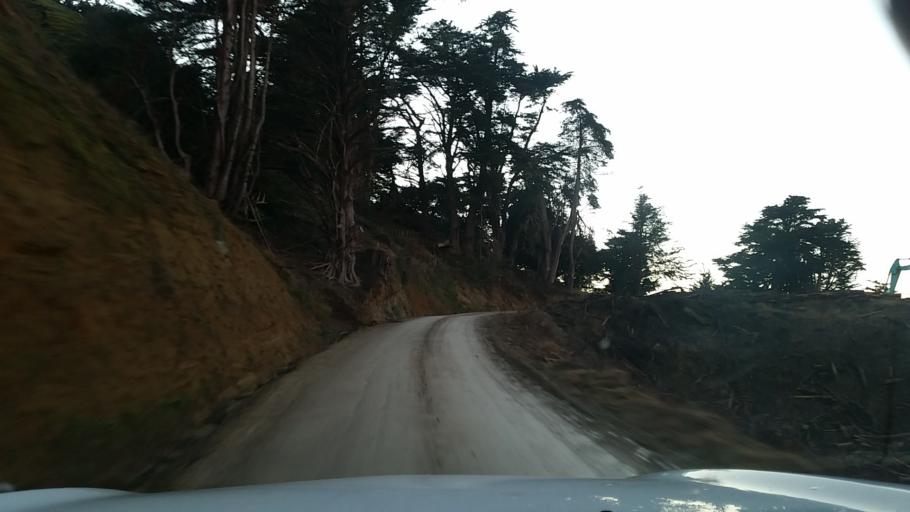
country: NZ
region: Manawatu-Wanganui
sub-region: Wanganui District
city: Wanganui
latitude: -39.7526
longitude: 174.8887
